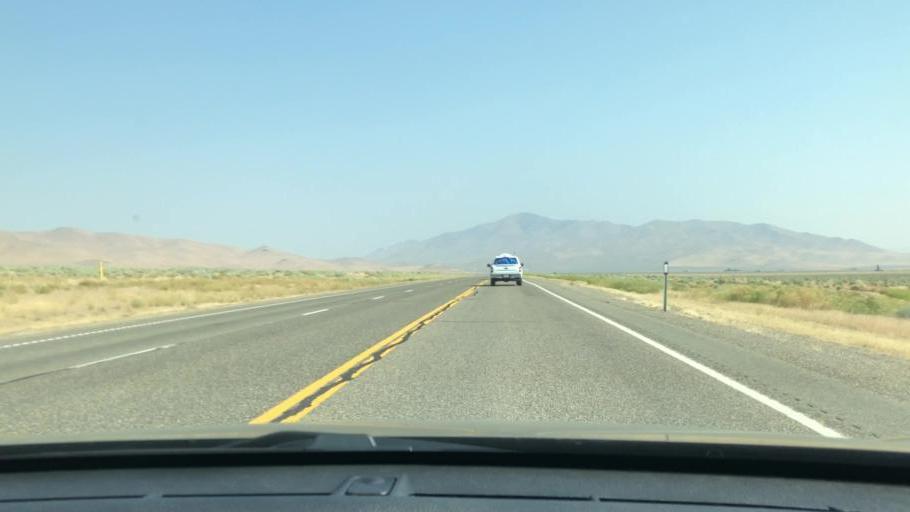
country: US
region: Nevada
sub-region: Humboldt County
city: Winnemucca
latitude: 41.2370
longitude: -117.6862
